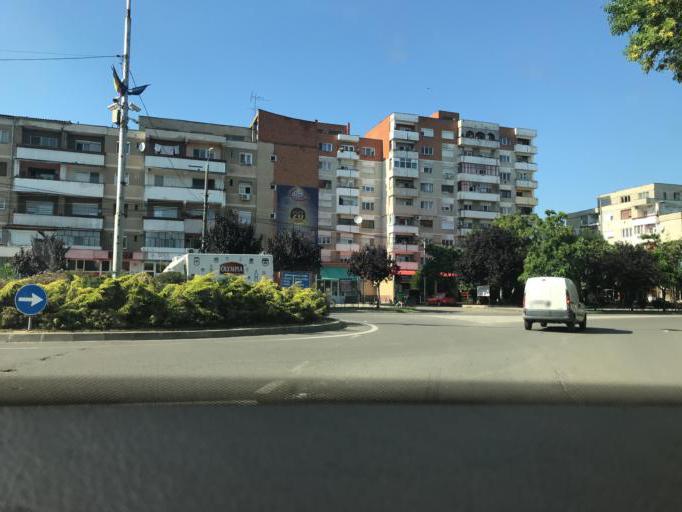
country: RO
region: Bihor
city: Margita
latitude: 47.3431
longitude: 22.3311
